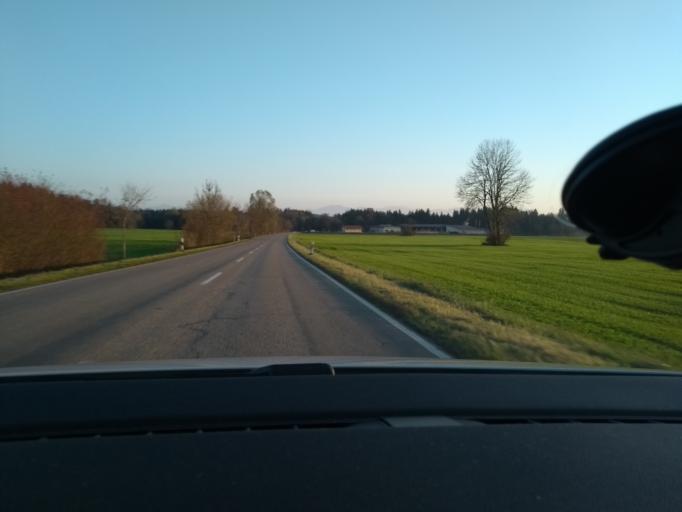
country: DE
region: Bavaria
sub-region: Upper Bavaria
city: Schonstett
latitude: 48.0101
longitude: 12.2453
